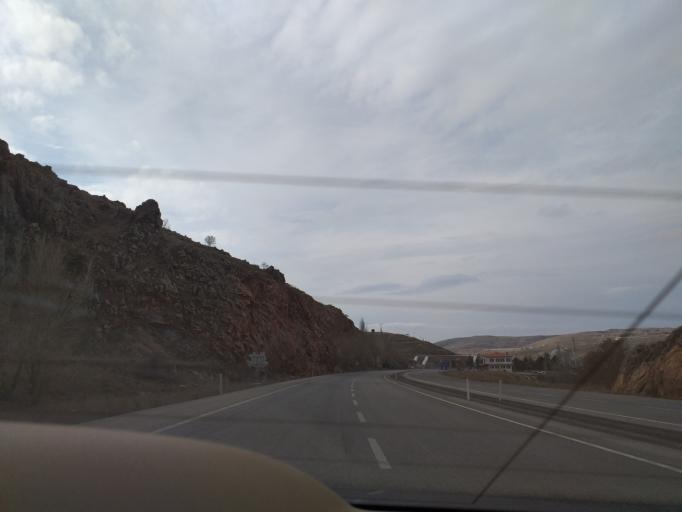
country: TR
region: Yozgat
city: Yozgat
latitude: 39.7999
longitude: 34.7667
